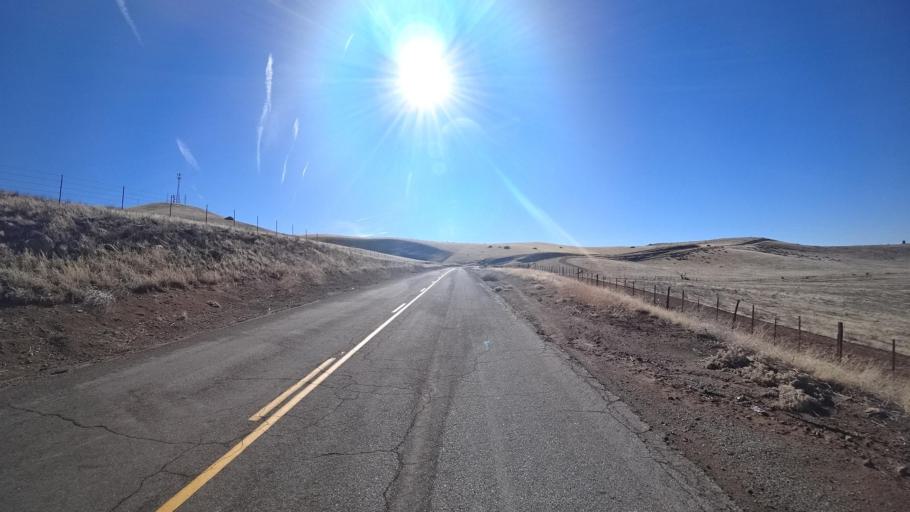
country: US
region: California
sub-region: Kern County
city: Maricopa
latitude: 34.9236
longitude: -119.4099
